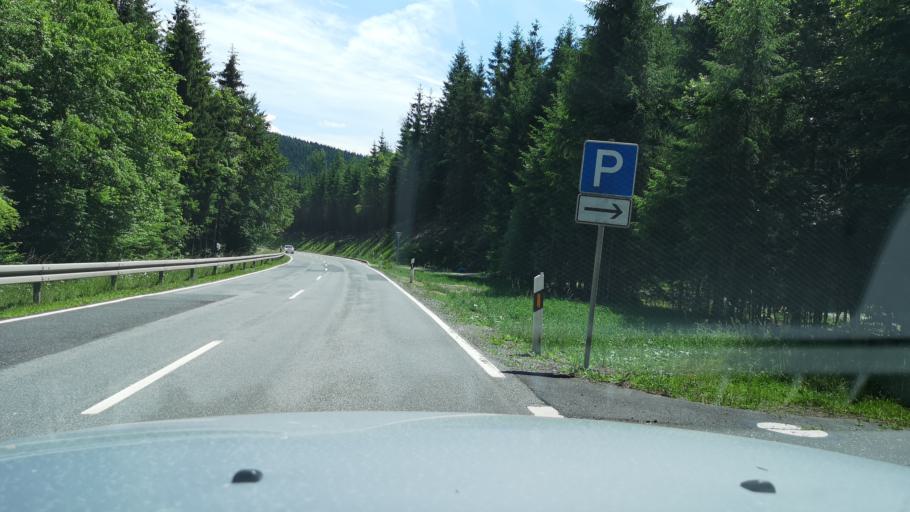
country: DE
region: Bavaria
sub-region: Upper Franconia
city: Tschirn
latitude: 50.3977
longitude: 11.4828
